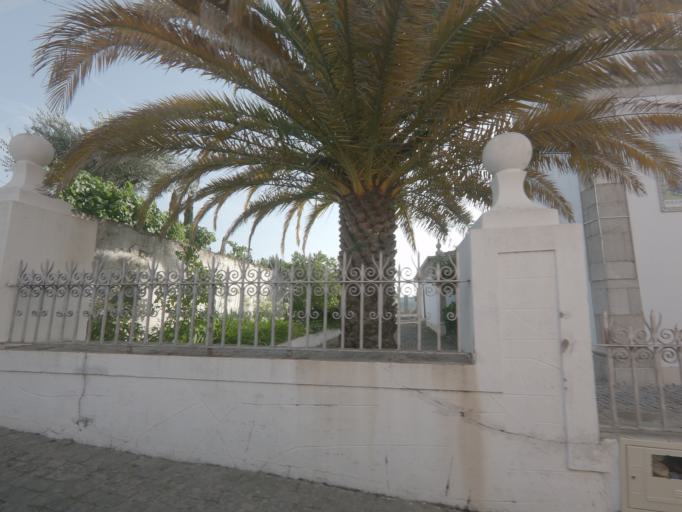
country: PT
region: Viseu
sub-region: Sao Joao da Pesqueira
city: Sao Joao da Pesqueira
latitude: 41.2270
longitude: -7.4666
